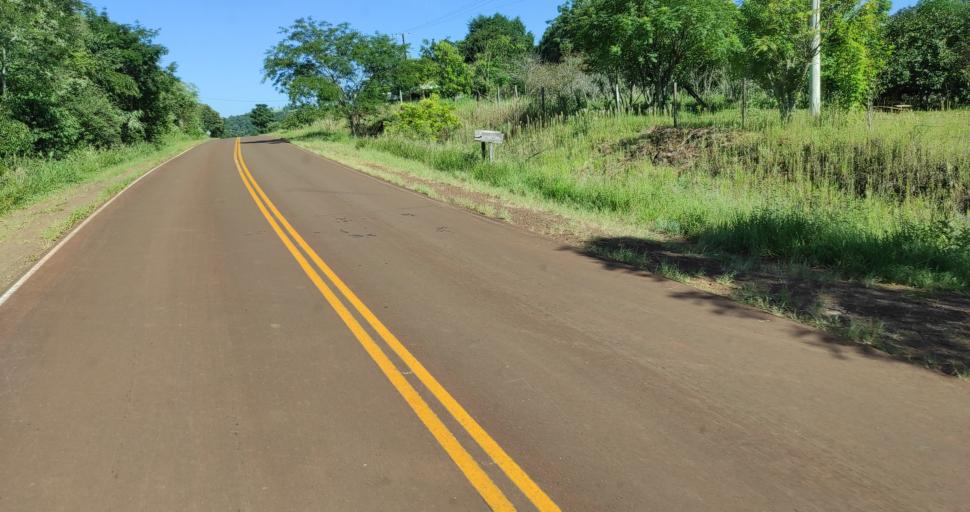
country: AR
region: Misiones
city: El Soberbio
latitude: -27.2254
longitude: -54.0611
